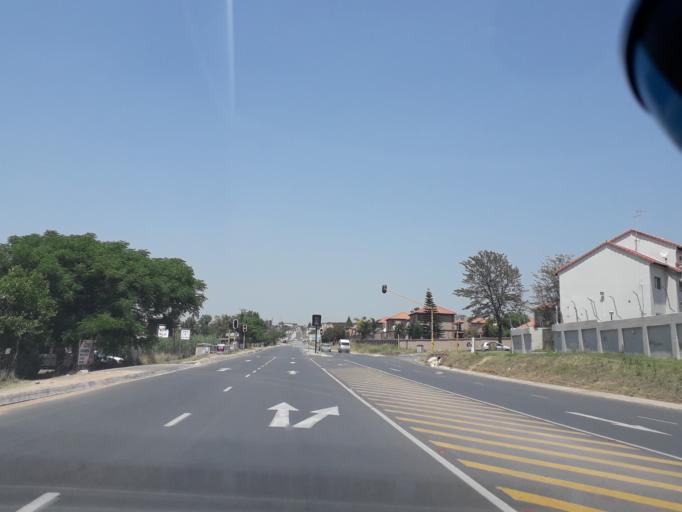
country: ZA
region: Gauteng
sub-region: City of Johannesburg Metropolitan Municipality
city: Midrand
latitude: -25.9643
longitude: 28.1216
